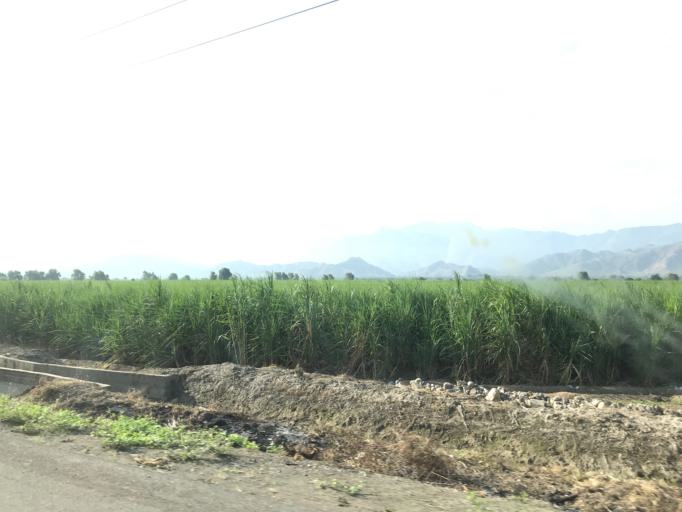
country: PE
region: Lambayeque
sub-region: Provincia de Chiclayo
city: Chongoyape
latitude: -6.6765
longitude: -79.4435
